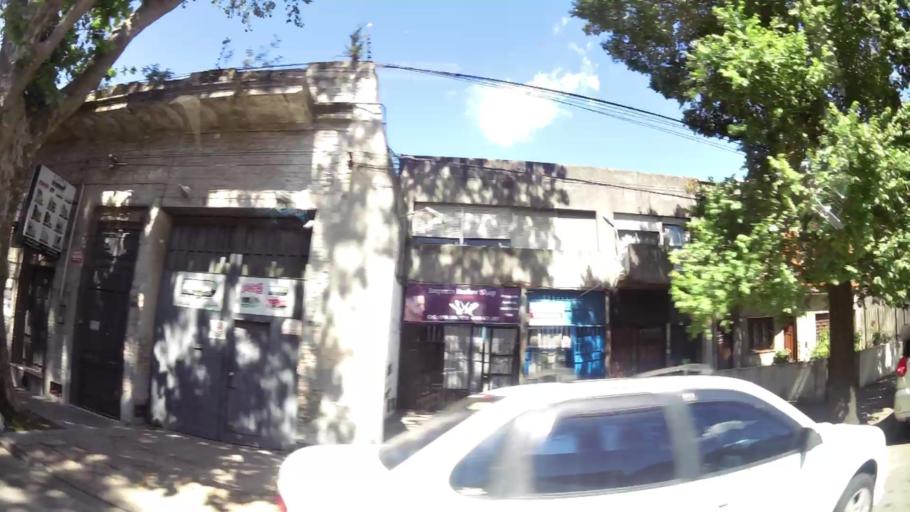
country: UY
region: Montevideo
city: Montevideo
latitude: -34.8977
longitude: -56.1840
